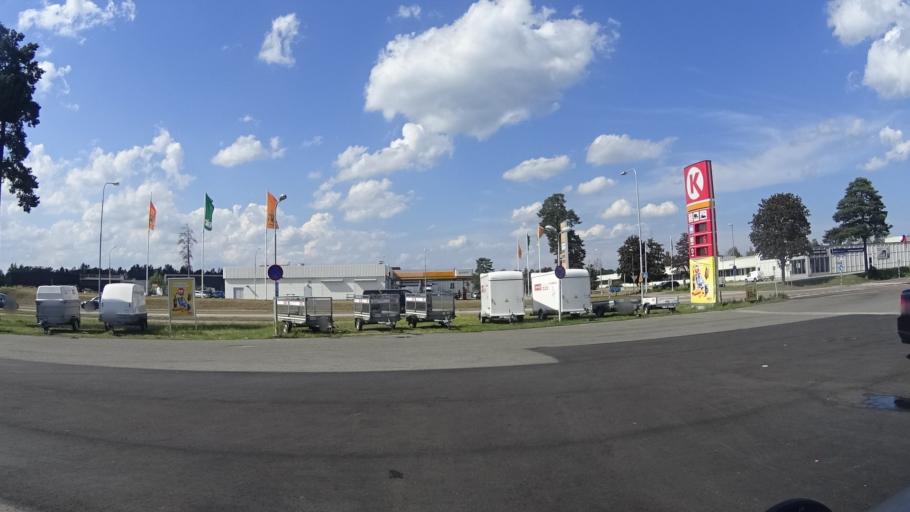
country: SE
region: Kalmar
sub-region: Oskarshamns Kommun
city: Oskarshamn
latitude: 57.2515
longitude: 16.4487
